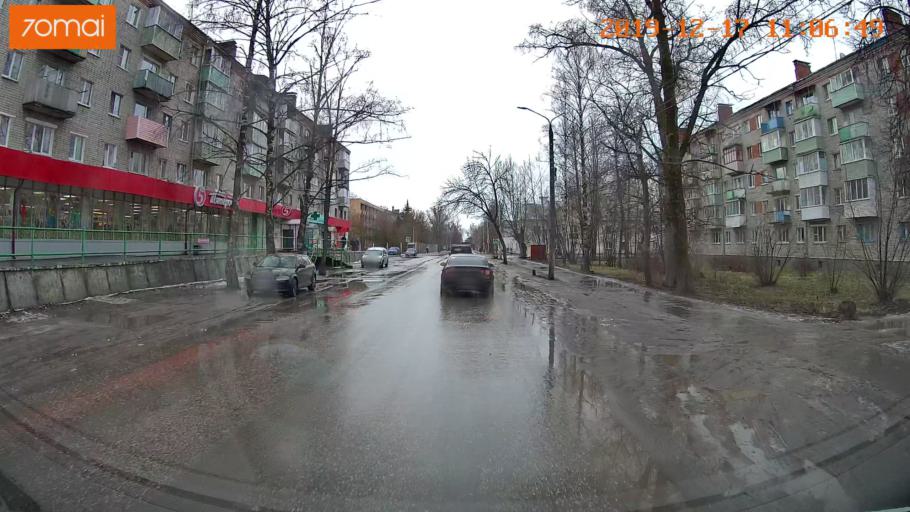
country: RU
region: Vladimir
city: Gus'-Khrustal'nyy
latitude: 55.6139
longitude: 40.6446
